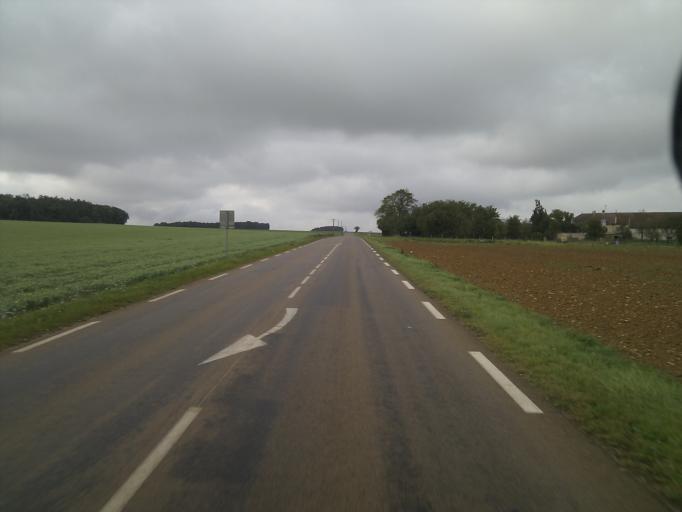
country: FR
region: Champagne-Ardenne
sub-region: Departement de la Haute-Marne
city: Doulaincourt-Saucourt
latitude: 48.2278
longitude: 5.2891
